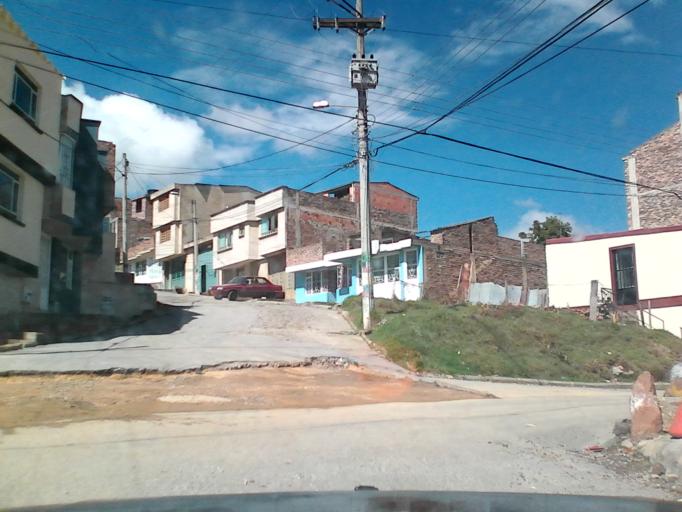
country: CO
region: Boyaca
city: Duitama
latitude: 5.8301
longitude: -73.0401
